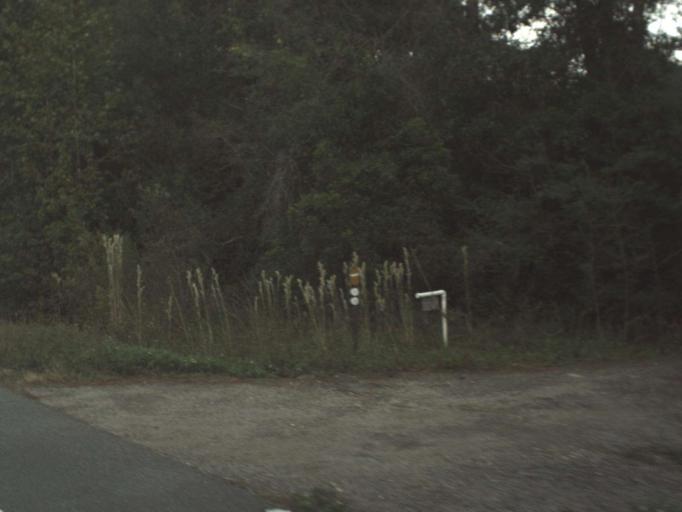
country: US
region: Florida
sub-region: Wakulla County
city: Crawfordville
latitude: 30.0160
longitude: -84.5011
